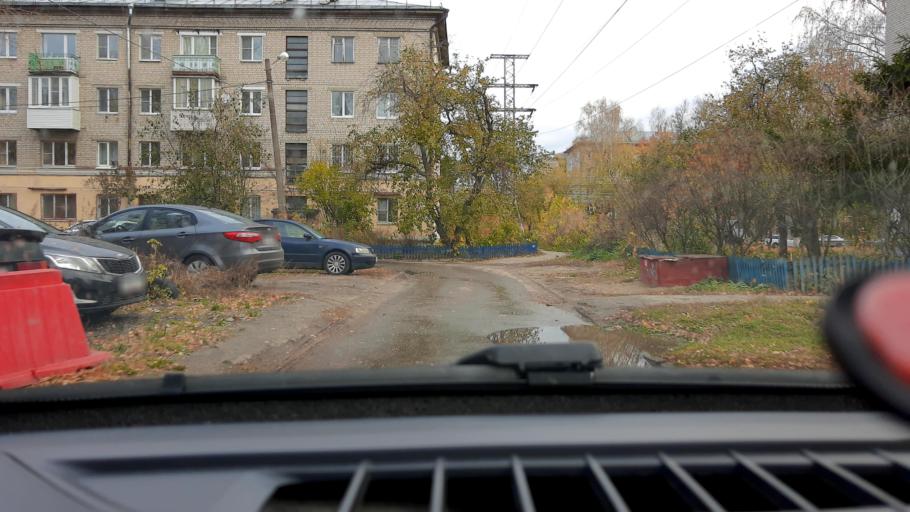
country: RU
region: Nizjnij Novgorod
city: Nizhniy Novgorod
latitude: 56.3192
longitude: 43.8885
